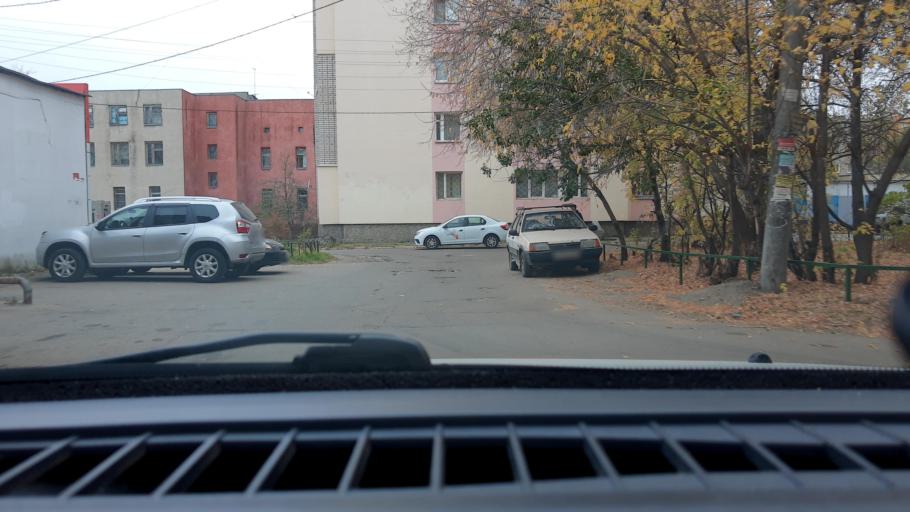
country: RU
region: Nizjnij Novgorod
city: Gorbatovka
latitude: 56.3580
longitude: 43.8108
